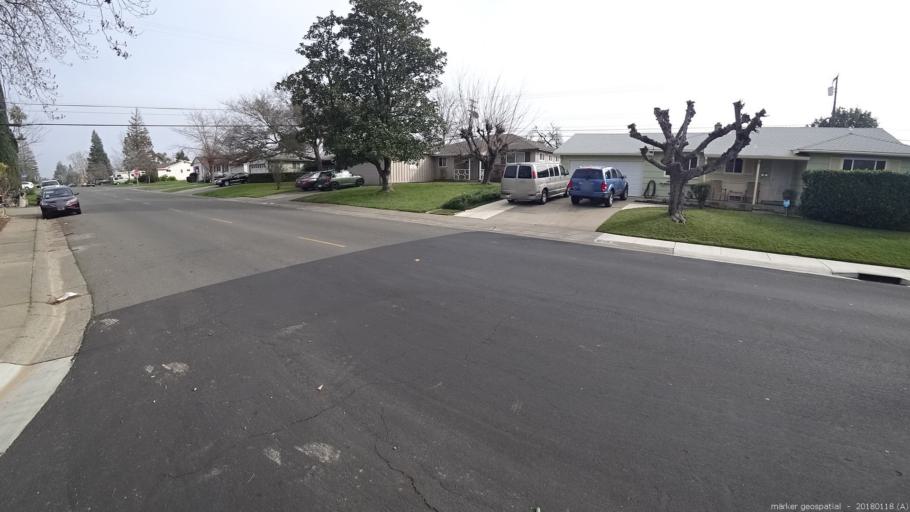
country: US
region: California
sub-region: Sacramento County
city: Rancho Cordova
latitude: 38.5895
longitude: -121.3074
